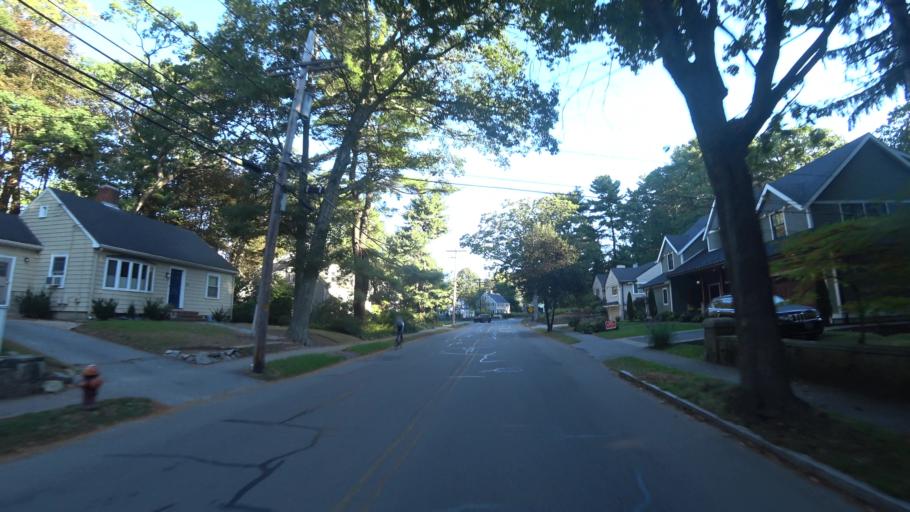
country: US
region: Massachusetts
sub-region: Middlesex County
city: Newton
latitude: 42.3334
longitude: -71.1883
